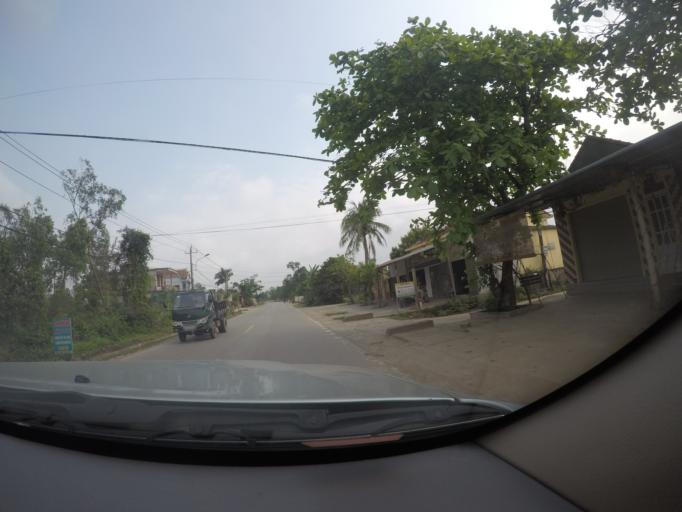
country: VN
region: Quang Binh
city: Kwang Binh
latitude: 17.4637
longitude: 106.5598
